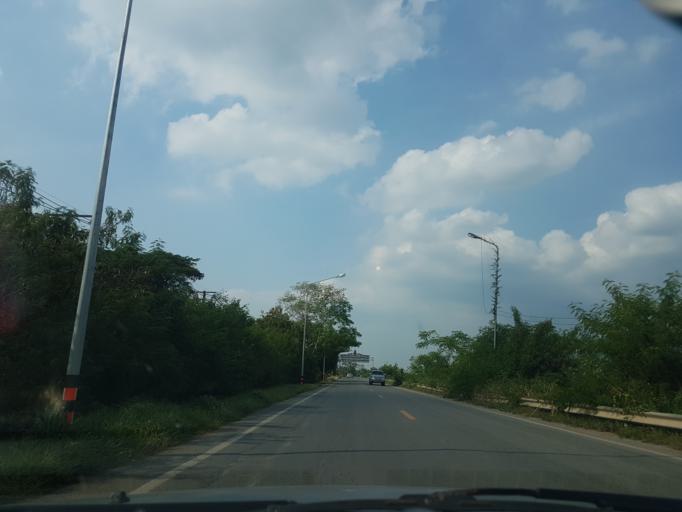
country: TH
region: Phra Nakhon Si Ayutthaya
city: Phachi
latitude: 14.4003
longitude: 100.7906
